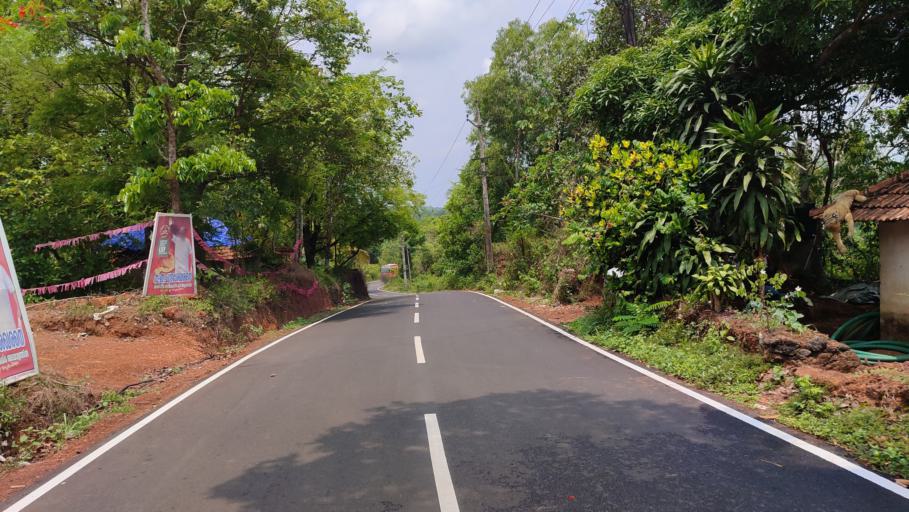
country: IN
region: Kerala
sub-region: Kasaragod District
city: Kannangad
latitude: 12.3209
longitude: 75.1364
